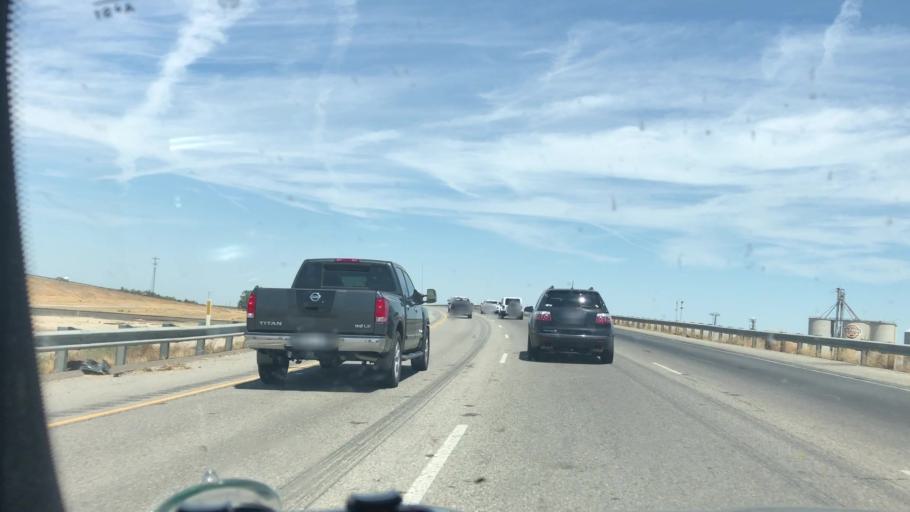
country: US
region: California
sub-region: Kern County
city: McFarland
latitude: 35.5911
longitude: -119.2047
